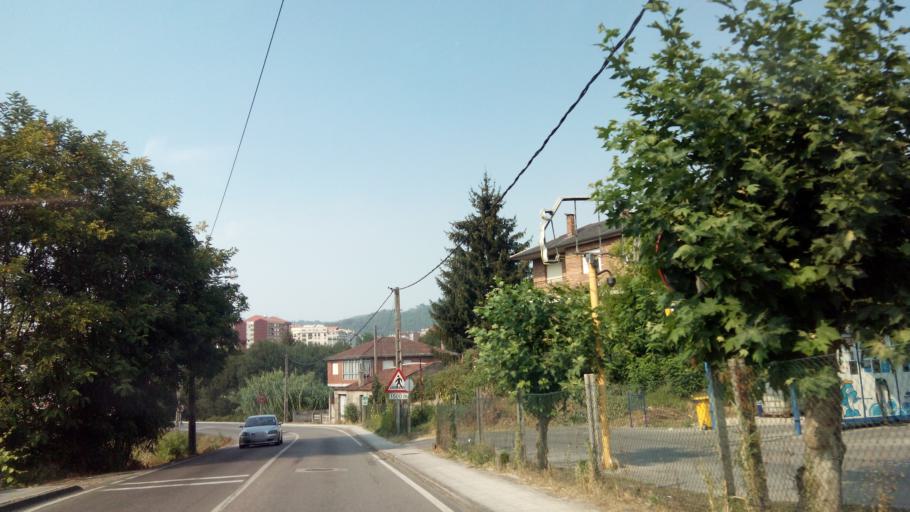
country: ES
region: Galicia
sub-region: Provincia de Pontevedra
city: Ponteareas
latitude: 42.1661
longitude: -8.5057
